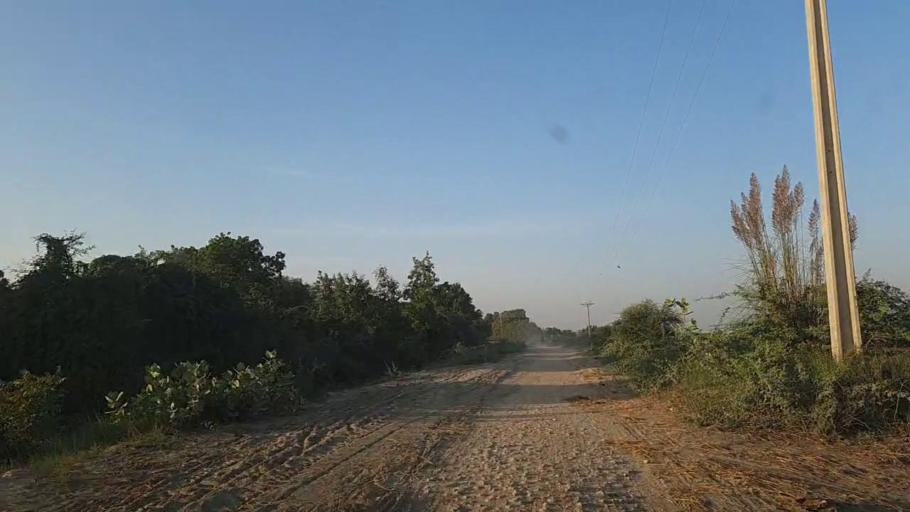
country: PK
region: Sindh
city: Mirpur Batoro
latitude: 24.7218
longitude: 68.2139
